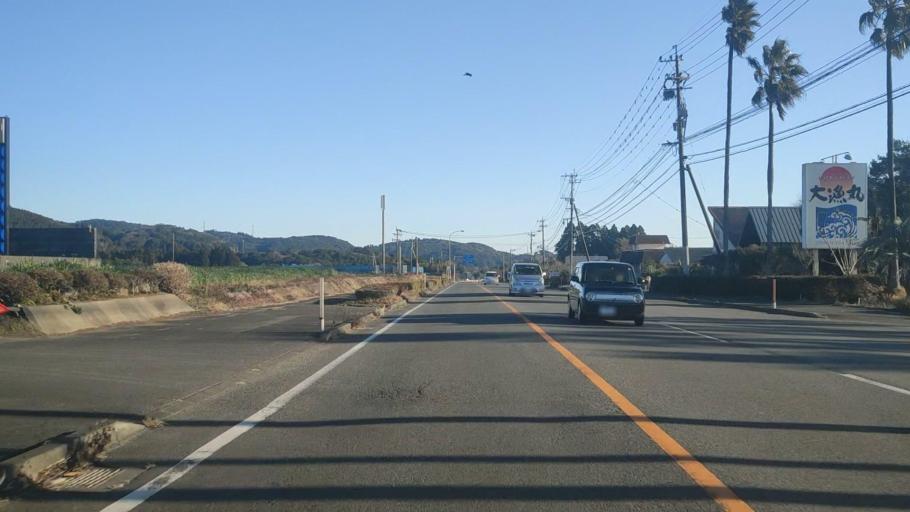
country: JP
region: Miyazaki
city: Takanabe
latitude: 32.3255
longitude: 131.5994
